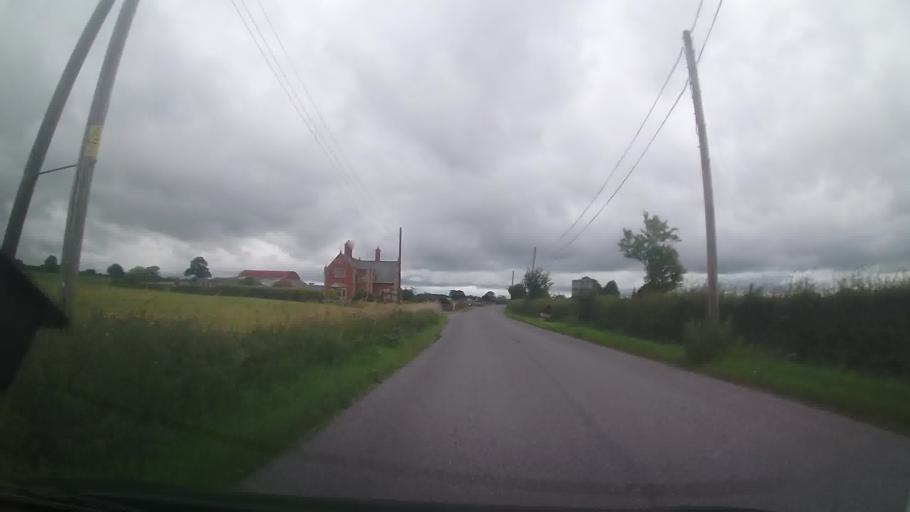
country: GB
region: England
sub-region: Shropshire
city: Petton
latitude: 52.8420
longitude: -2.8255
